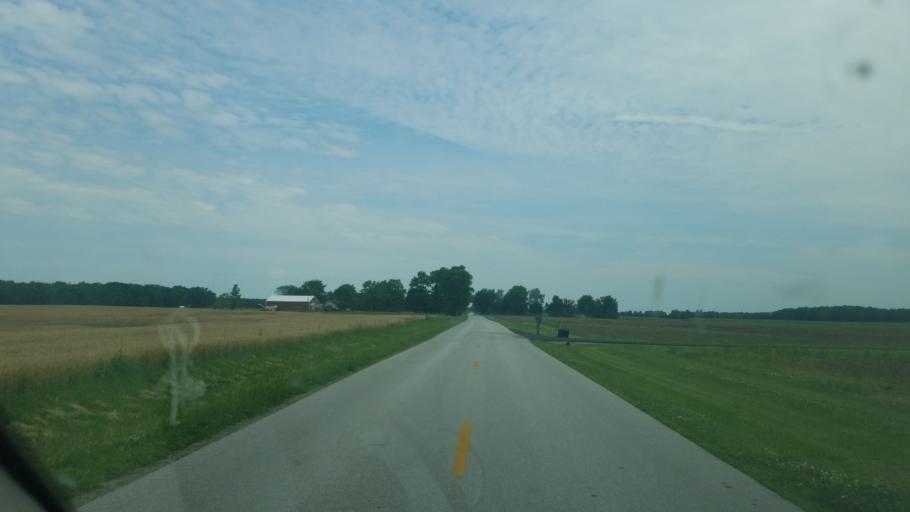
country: US
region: Ohio
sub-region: Wyandot County
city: Carey
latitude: 41.0465
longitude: -83.4392
